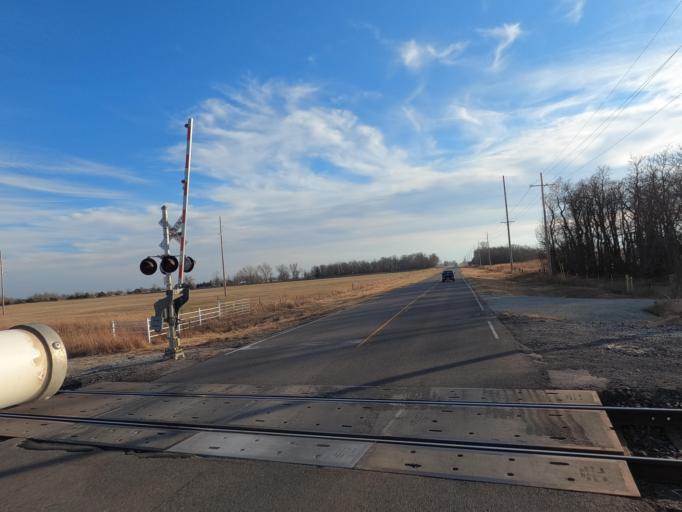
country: US
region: Kansas
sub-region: Reno County
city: Buhler
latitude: 38.0366
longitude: -97.7753
